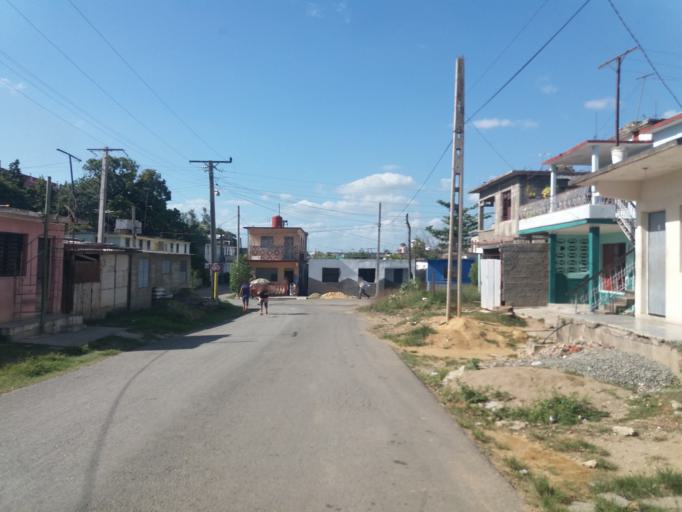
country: CU
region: Cienfuegos
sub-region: Municipio de Cienfuegos
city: Cienfuegos
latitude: 22.1536
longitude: -80.4315
